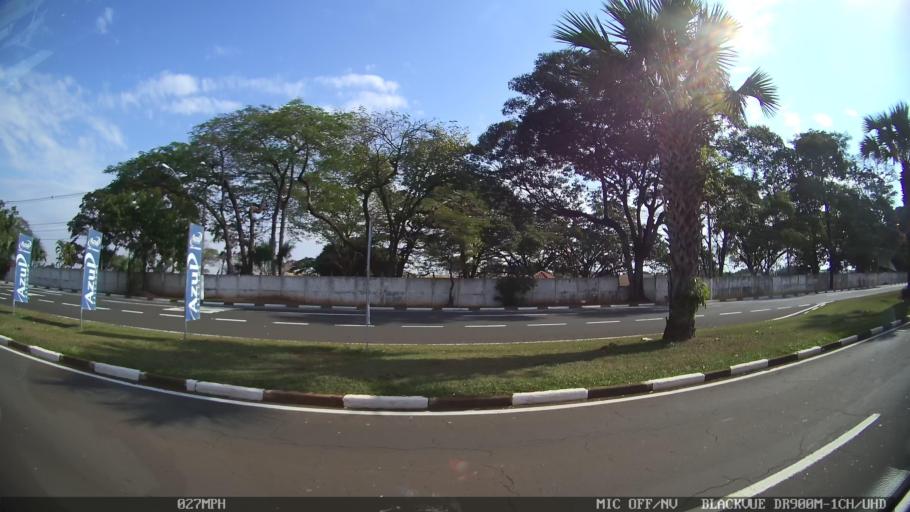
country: BR
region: Sao Paulo
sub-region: Paulinia
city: Paulinia
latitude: -22.7820
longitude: -47.1422
